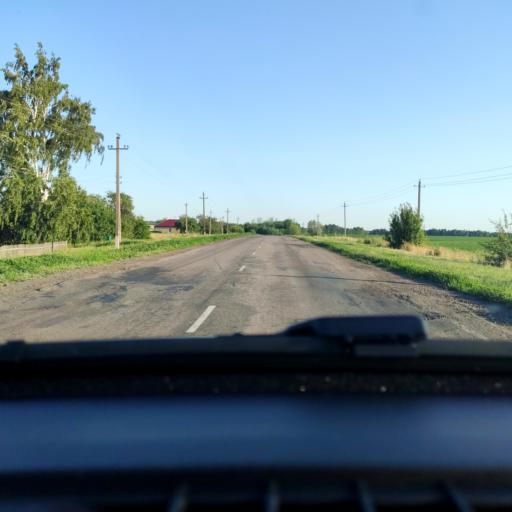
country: RU
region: Voronezj
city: Kashirskoye
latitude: 51.5072
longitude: 39.8322
